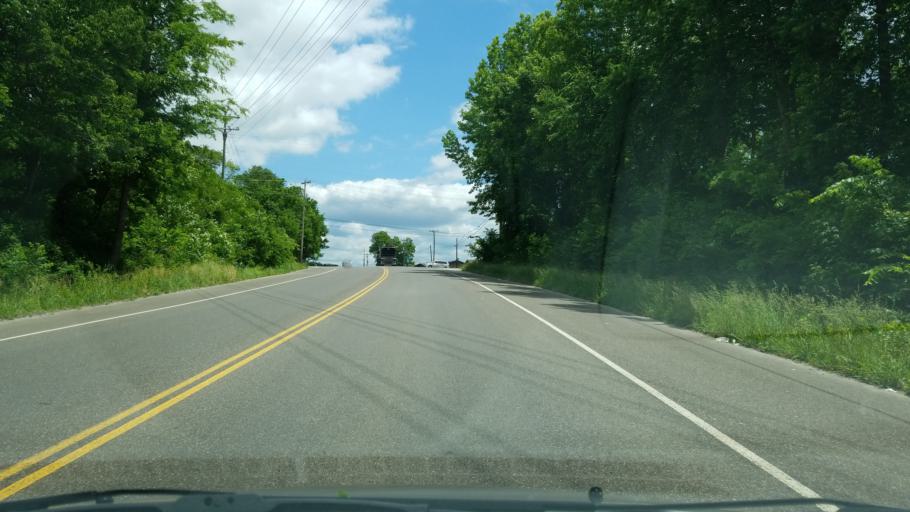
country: US
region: Tennessee
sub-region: Rhea County
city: Dayton
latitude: 35.4987
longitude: -85.0210
